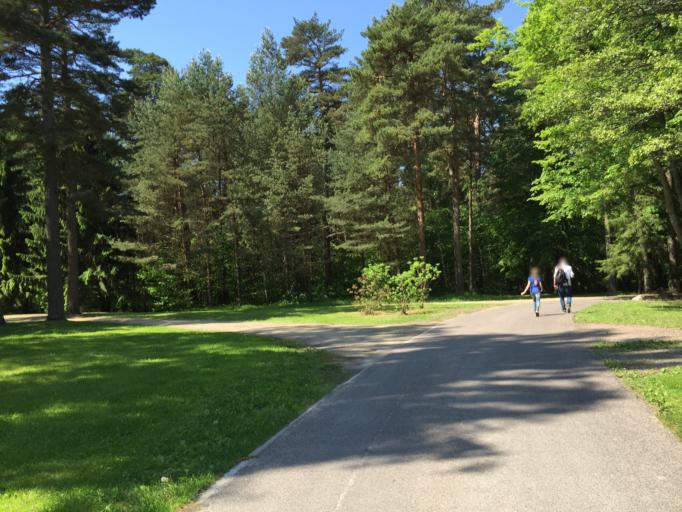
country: LT
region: Klaipedos apskritis
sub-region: Klaipeda
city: Palanga
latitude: 55.9037
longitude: 21.0598
